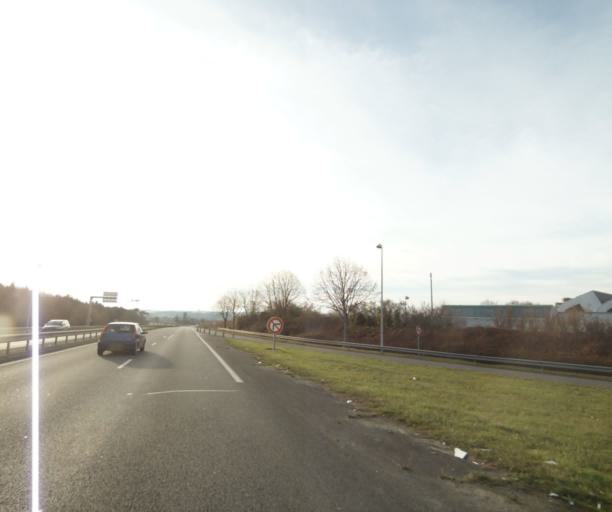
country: FR
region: Poitou-Charentes
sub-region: Departement de la Charente-Maritime
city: Les Gonds
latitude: 45.7334
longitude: -0.6122
